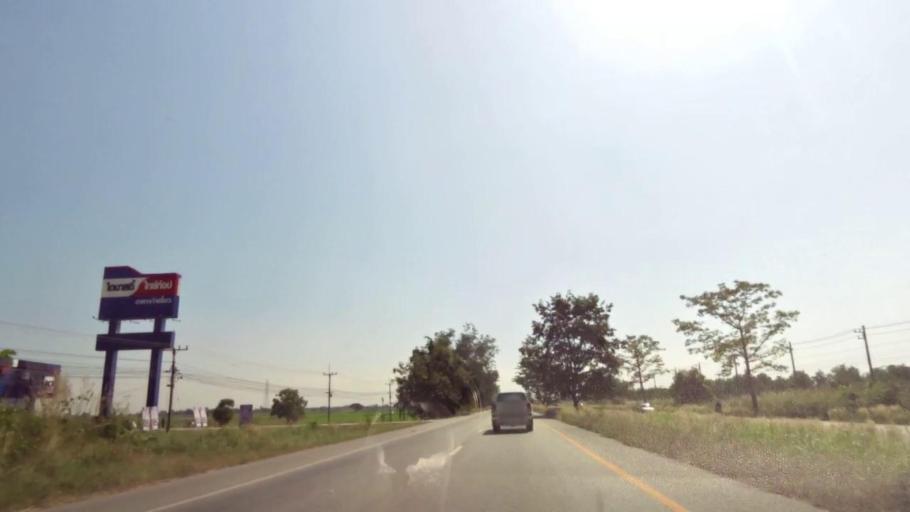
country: TH
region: Nakhon Sawan
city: Kao Liao
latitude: 15.8362
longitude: 100.1176
